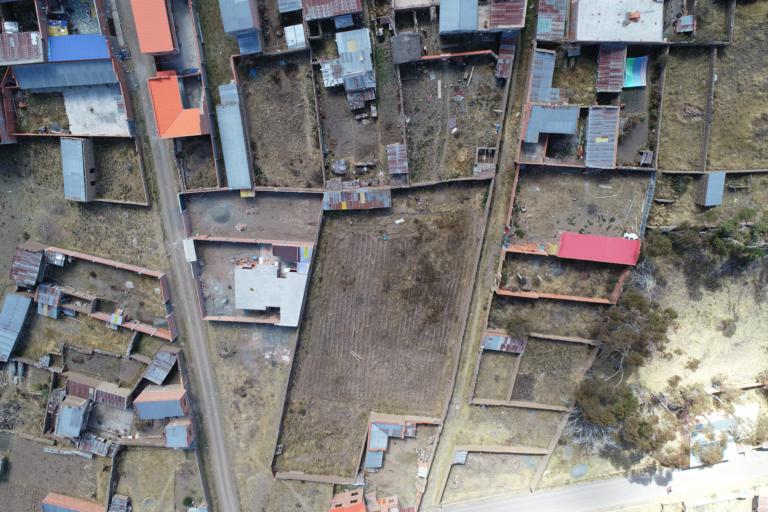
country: BO
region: La Paz
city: Achacachi
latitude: -15.8973
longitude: -68.9075
